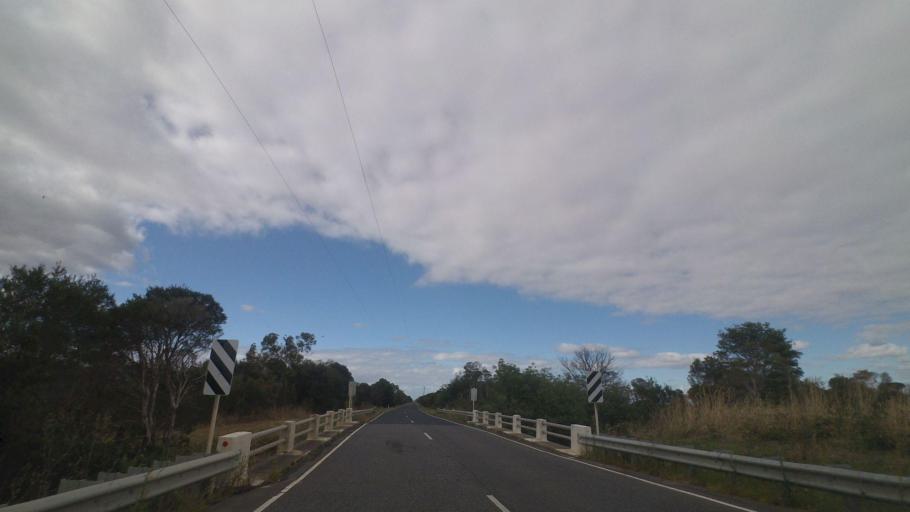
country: AU
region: Victoria
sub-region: Cardinia
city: Pakenham South
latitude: -38.1153
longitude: 145.5630
